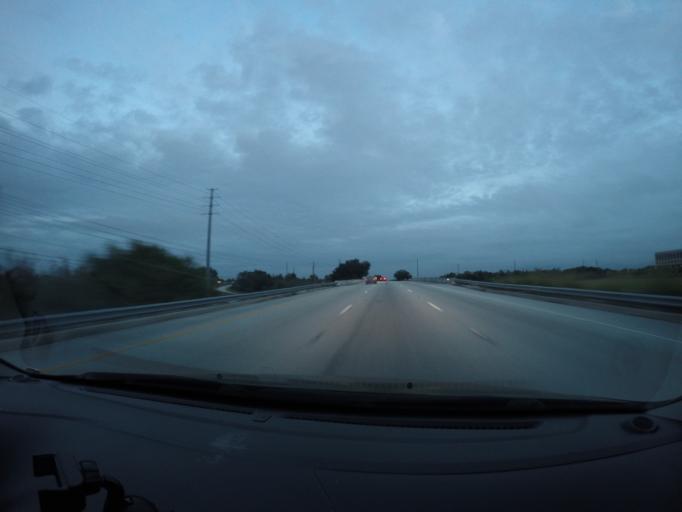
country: US
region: Florida
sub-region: Orange County
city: Tangelo Park
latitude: 28.4500
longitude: -81.4601
